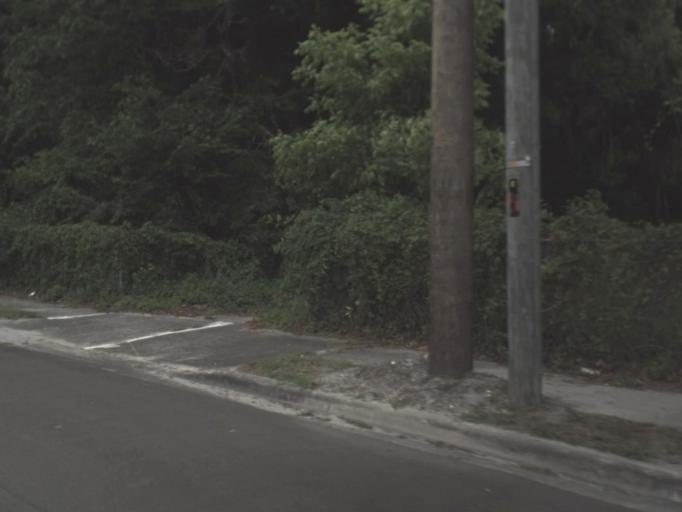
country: US
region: Florida
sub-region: Alachua County
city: Waldo
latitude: 29.7930
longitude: -82.1662
